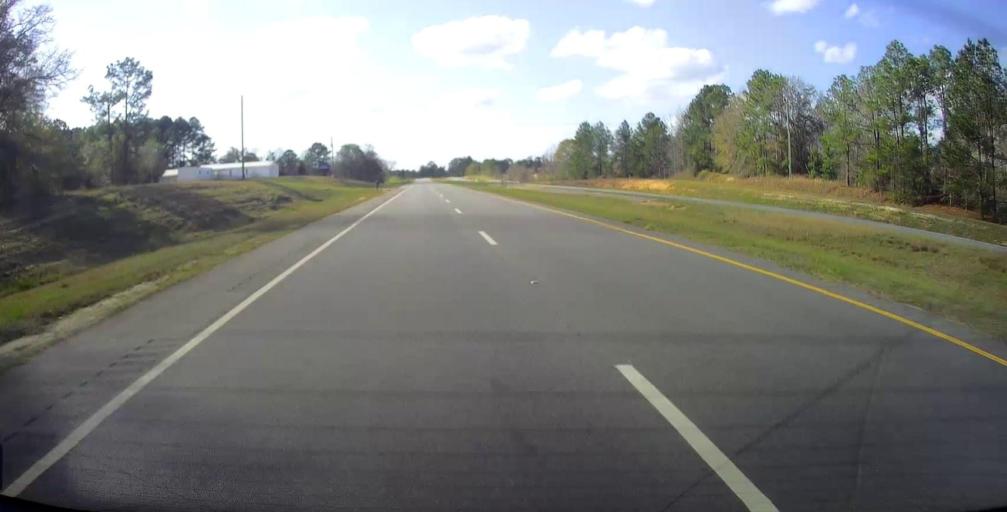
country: US
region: Georgia
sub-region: Telfair County
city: Helena
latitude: 32.0987
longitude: -82.9526
